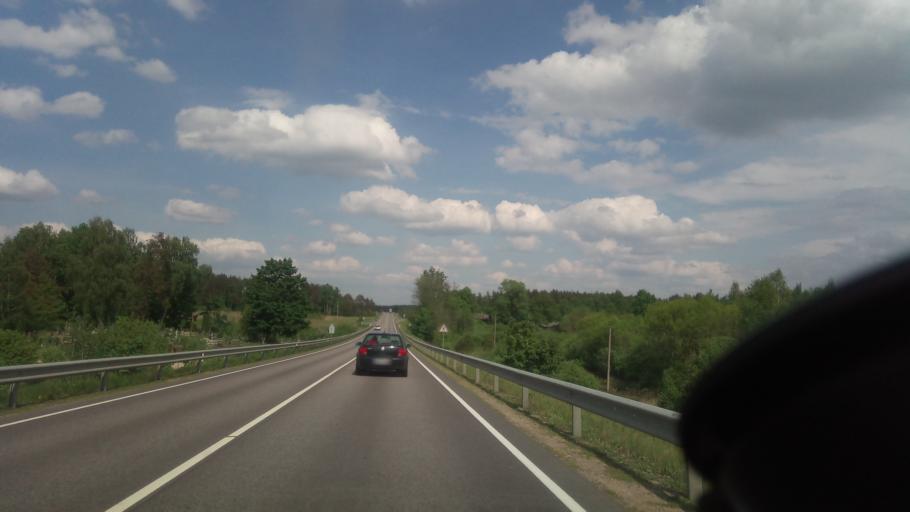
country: LT
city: Trakai
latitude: 54.6102
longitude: 24.8743
